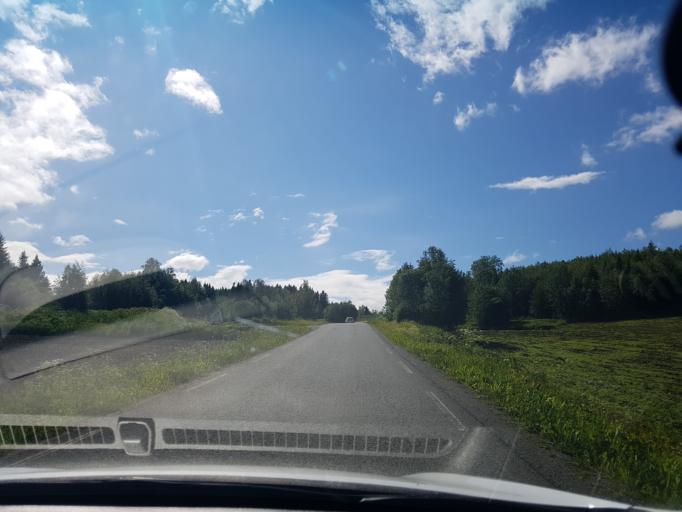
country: NO
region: Nord-Trondelag
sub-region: Frosta
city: Frosta
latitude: 63.6045
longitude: 10.8300
